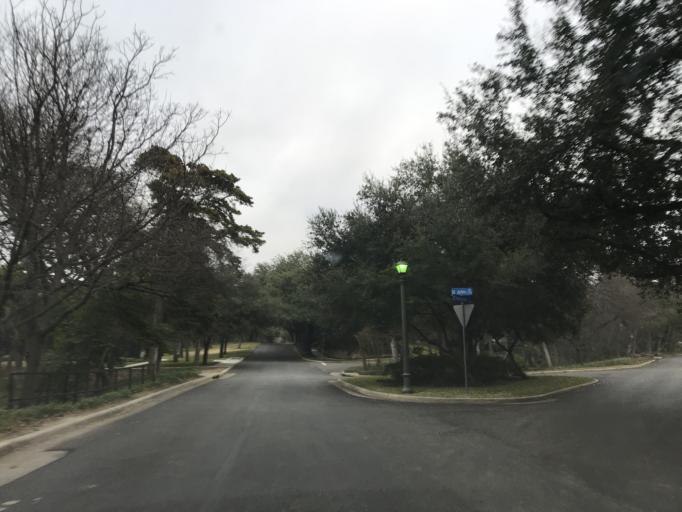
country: US
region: Texas
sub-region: Dallas County
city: Highland Park
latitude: 32.8245
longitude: -96.7979
